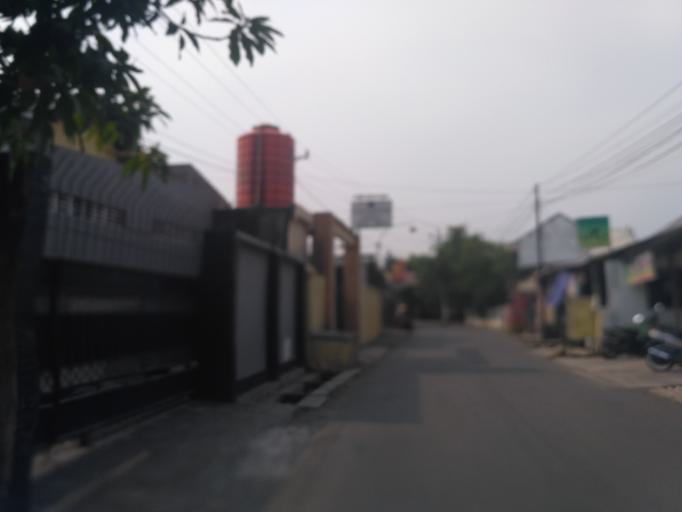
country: ID
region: Central Java
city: Mranggen
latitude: -7.0173
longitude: 110.4834
